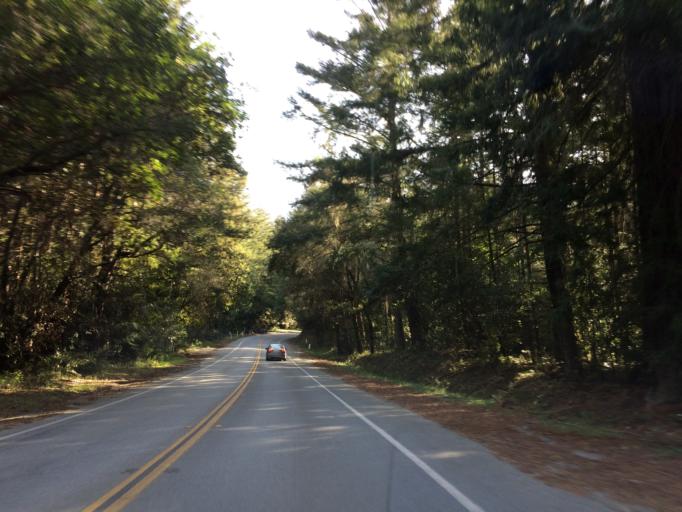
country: US
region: California
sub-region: Santa Cruz County
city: Felton
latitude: 37.0261
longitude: -122.0976
